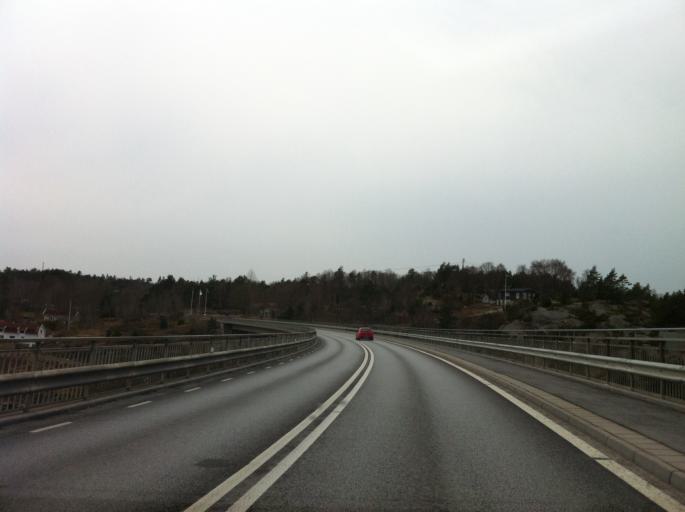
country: SE
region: Vaestra Goetaland
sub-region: Orust
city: Henan
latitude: 58.2931
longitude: 11.7039
